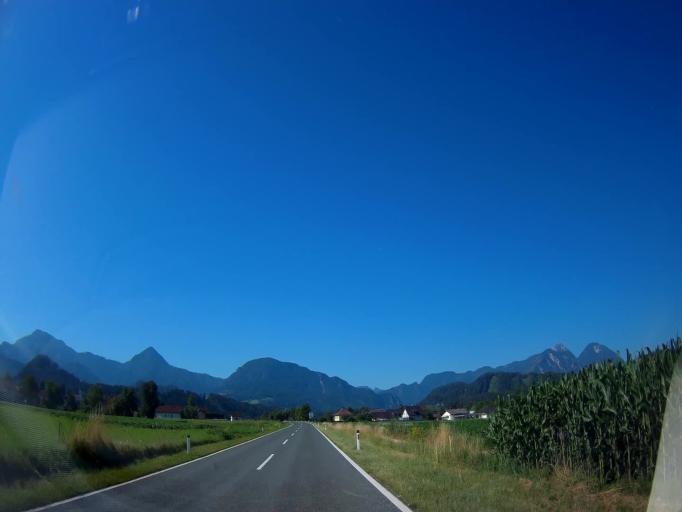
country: AT
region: Carinthia
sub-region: Politischer Bezirk Volkermarkt
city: Eberndorf
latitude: 46.5781
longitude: 14.6312
